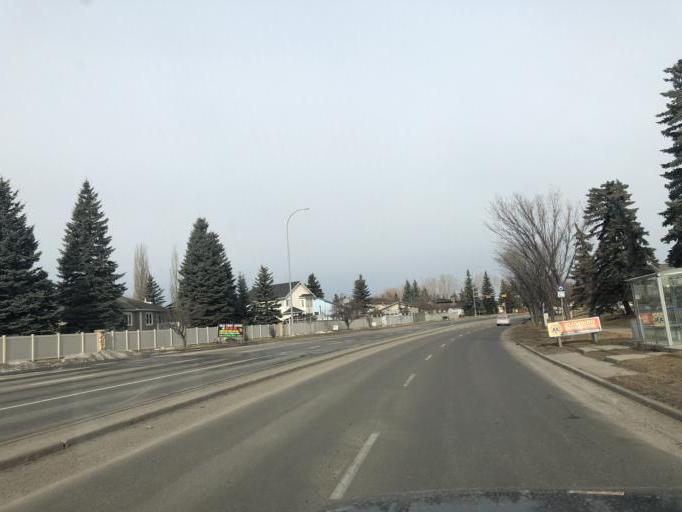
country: CA
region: Alberta
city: Calgary
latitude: 50.9433
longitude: -114.0031
